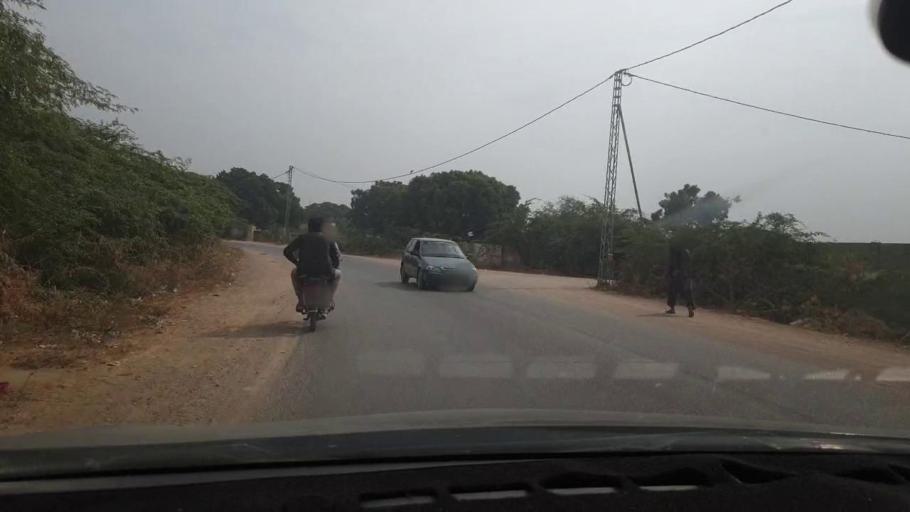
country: PK
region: Sindh
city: Malir Cantonment
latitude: 24.9142
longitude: 67.2617
